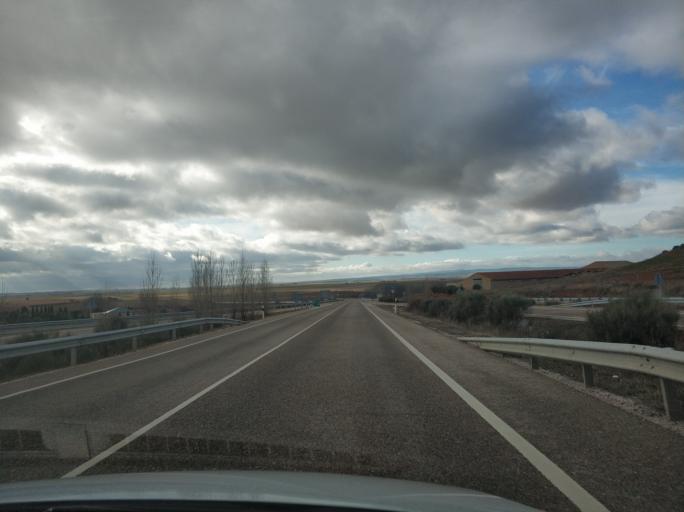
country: ES
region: Castille and Leon
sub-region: Provincia de Segovia
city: Ayllon
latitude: 41.4300
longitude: -3.3774
